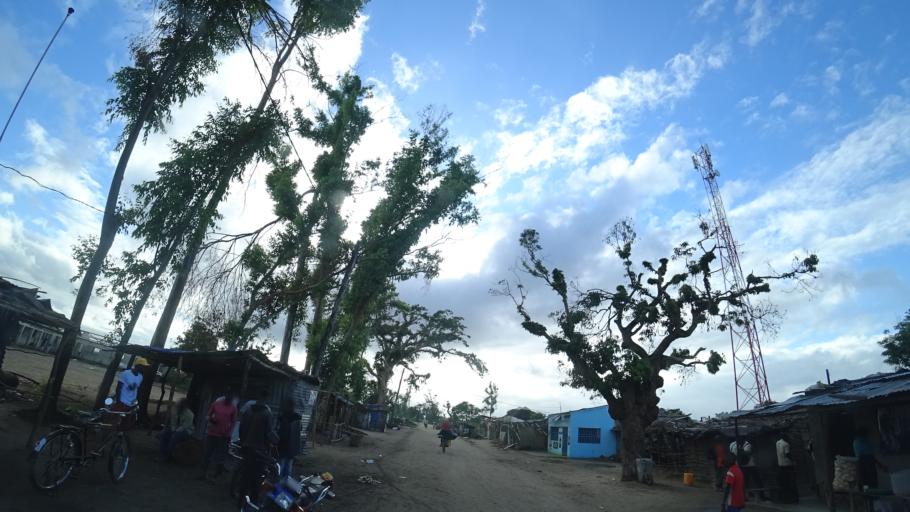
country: MZ
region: Sofala
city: Beira
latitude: -19.7161
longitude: 35.0074
